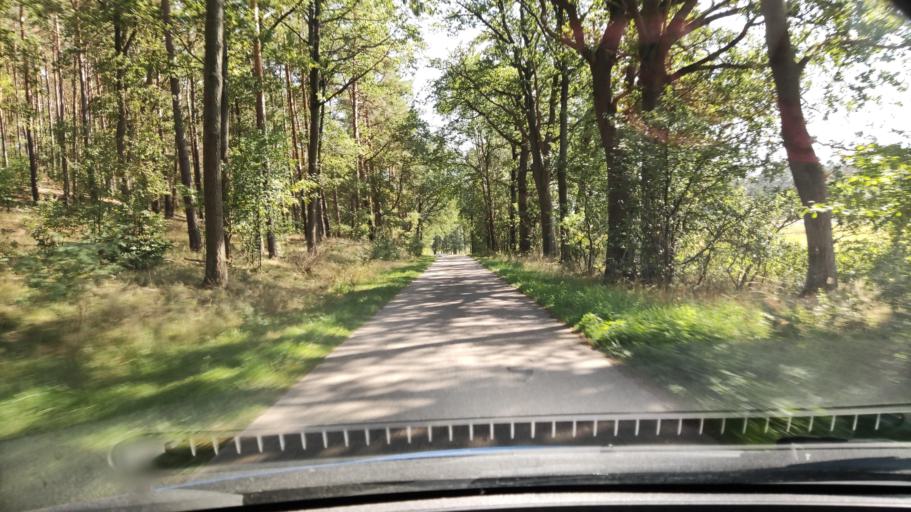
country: DE
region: Lower Saxony
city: Gohrde
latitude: 53.1416
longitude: 10.9450
